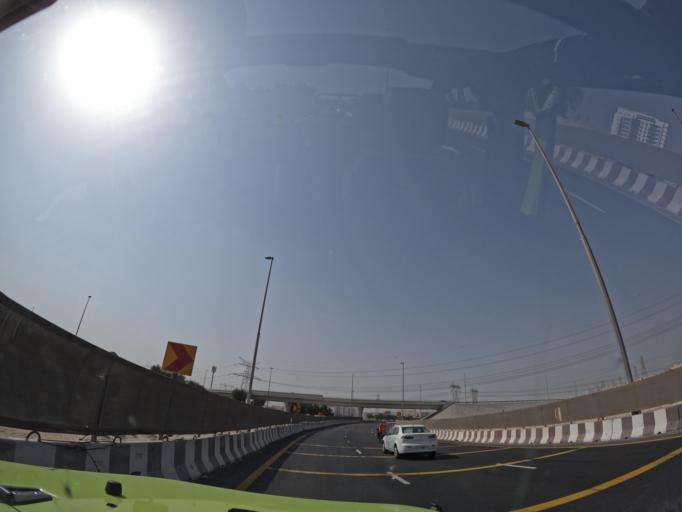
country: AE
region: Ash Shariqah
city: Sharjah
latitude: 25.1821
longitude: 55.3895
